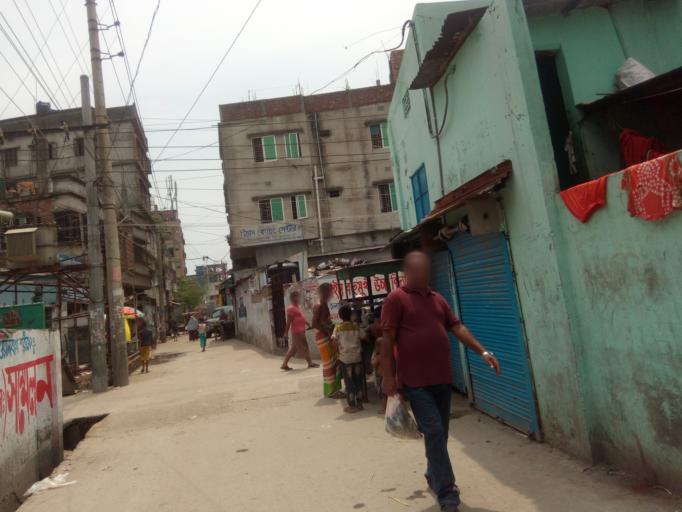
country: BD
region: Dhaka
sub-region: Dhaka
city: Dhaka
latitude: 23.6908
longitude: 90.4387
